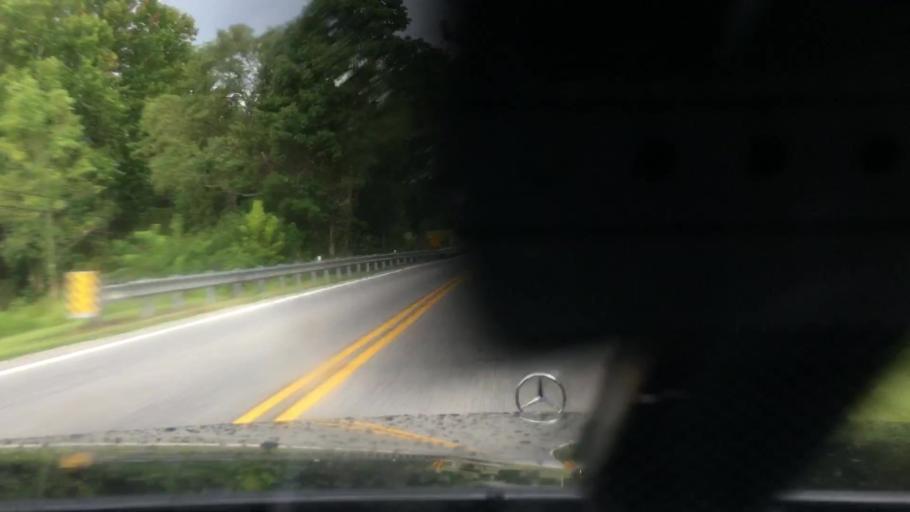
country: US
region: Virginia
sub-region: Nelson County
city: Lovingston
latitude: 37.7586
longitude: -78.9801
